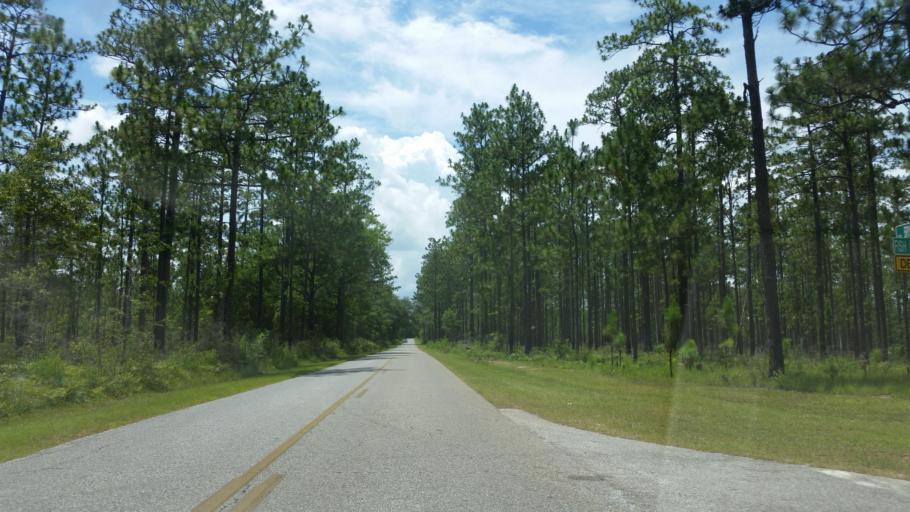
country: US
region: Florida
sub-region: Okaloosa County
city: Crestview
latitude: 30.7294
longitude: -86.8025
